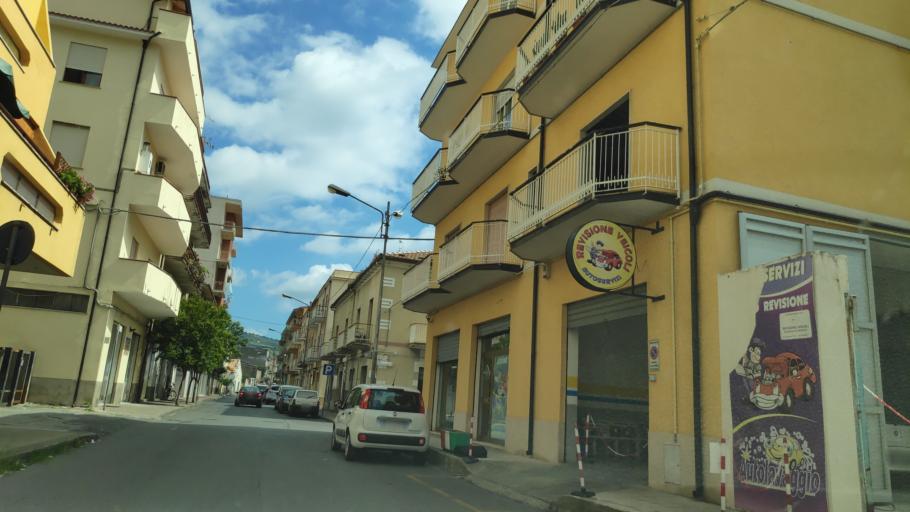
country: IT
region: Calabria
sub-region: Provincia di Cosenza
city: Amantea
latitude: 39.1340
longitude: 16.0722
